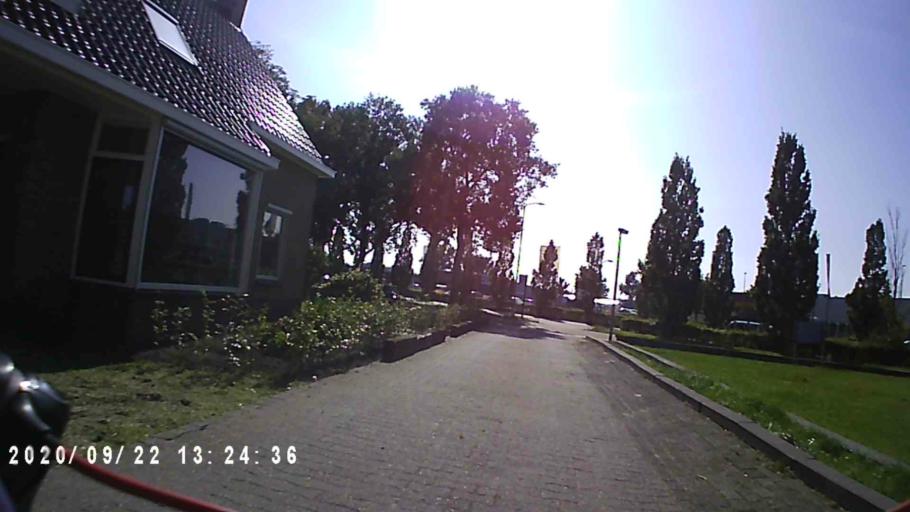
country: NL
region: Groningen
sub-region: Gemeente Leek
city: Leek
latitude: 53.1690
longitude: 6.3782
